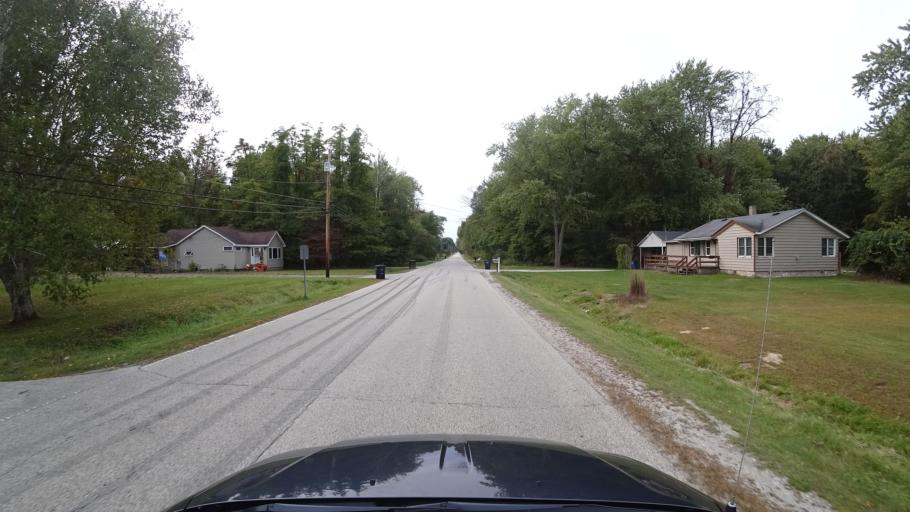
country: US
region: Indiana
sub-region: LaPorte County
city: Long Beach
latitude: 41.7381
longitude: -86.8181
